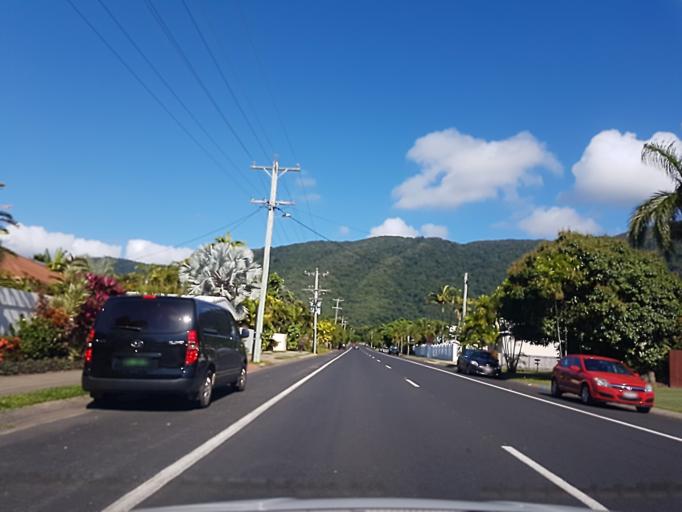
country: AU
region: Queensland
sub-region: Cairns
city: Palm Cove
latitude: -16.7448
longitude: 145.6668
